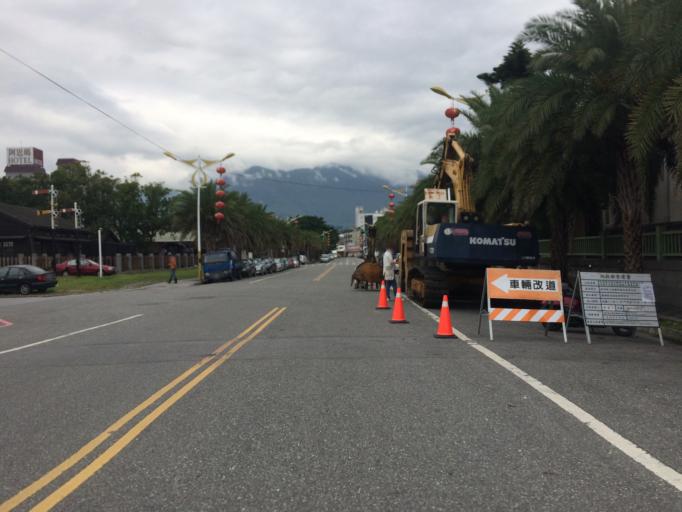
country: TW
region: Taiwan
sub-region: Hualien
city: Hualian
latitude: 23.9742
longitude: 121.6105
